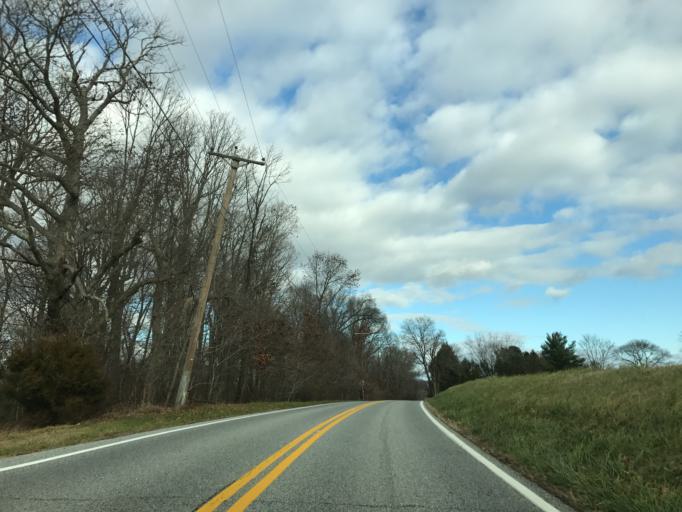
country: US
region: Pennsylvania
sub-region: York County
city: Stewartstown
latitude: 39.6554
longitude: -76.6093
